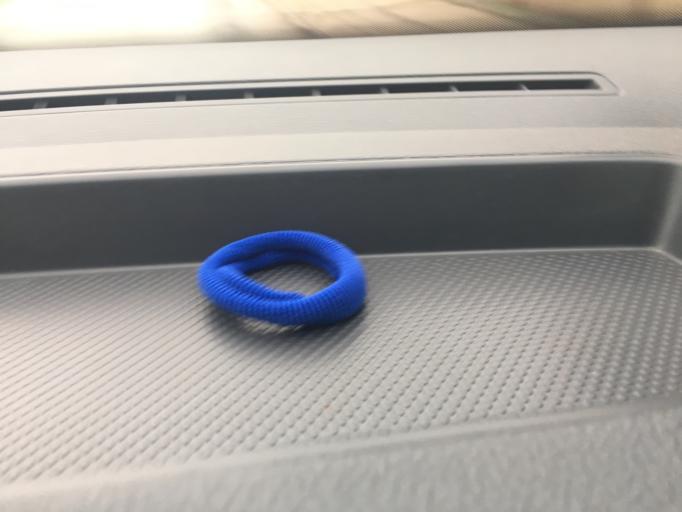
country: RS
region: Central Serbia
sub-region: Nisavski Okrug
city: Aleksinac
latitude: 43.5466
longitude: 21.7061
